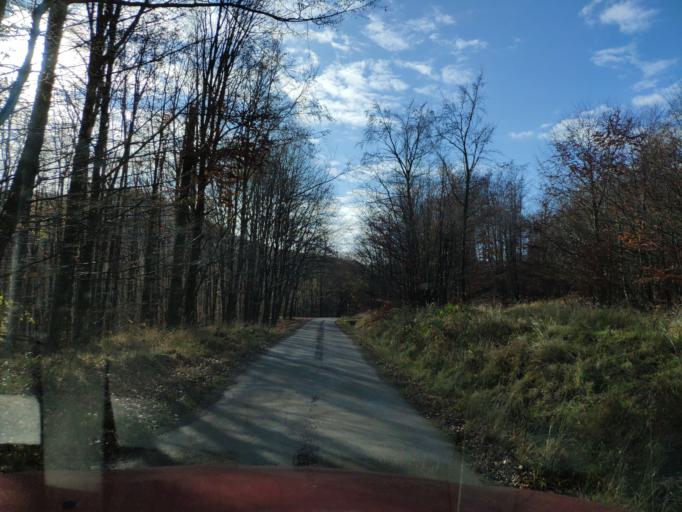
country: HU
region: Borsod-Abauj-Zemplen
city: Gonc
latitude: 48.6002
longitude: 21.4504
